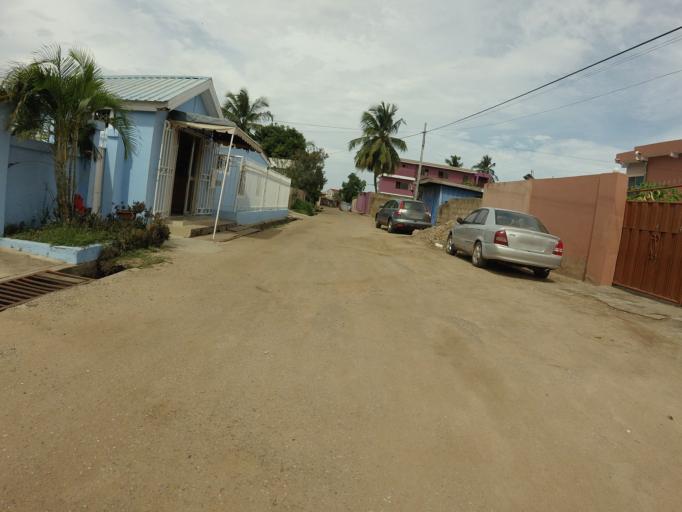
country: GH
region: Greater Accra
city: Accra
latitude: 5.5978
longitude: -0.2142
